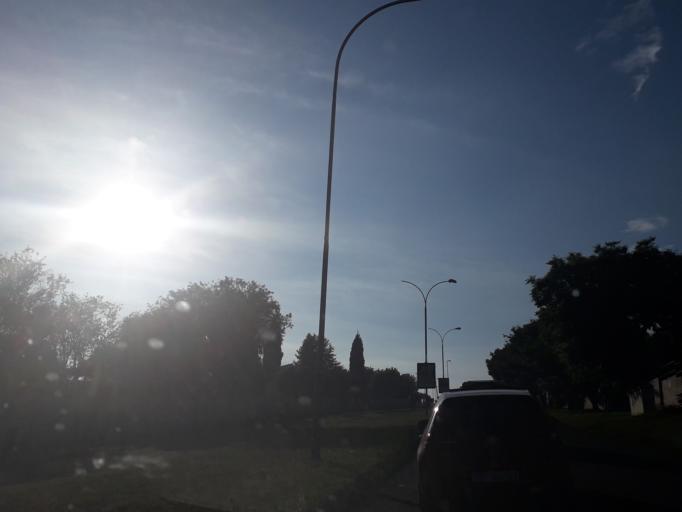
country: ZA
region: Gauteng
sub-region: City of Johannesburg Metropolitan Municipality
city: Roodepoort
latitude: -26.1028
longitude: 27.9214
